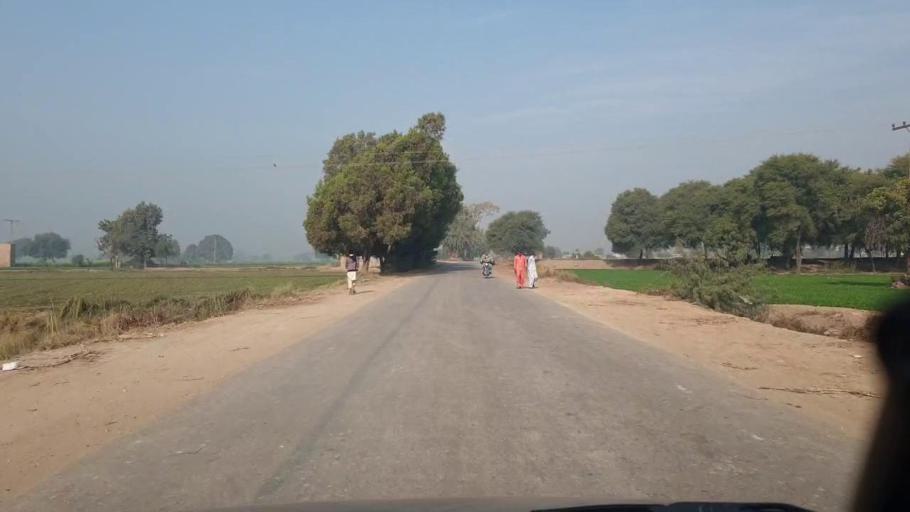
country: PK
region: Sindh
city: Shahdadpur
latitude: 25.9355
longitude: 68.6078
